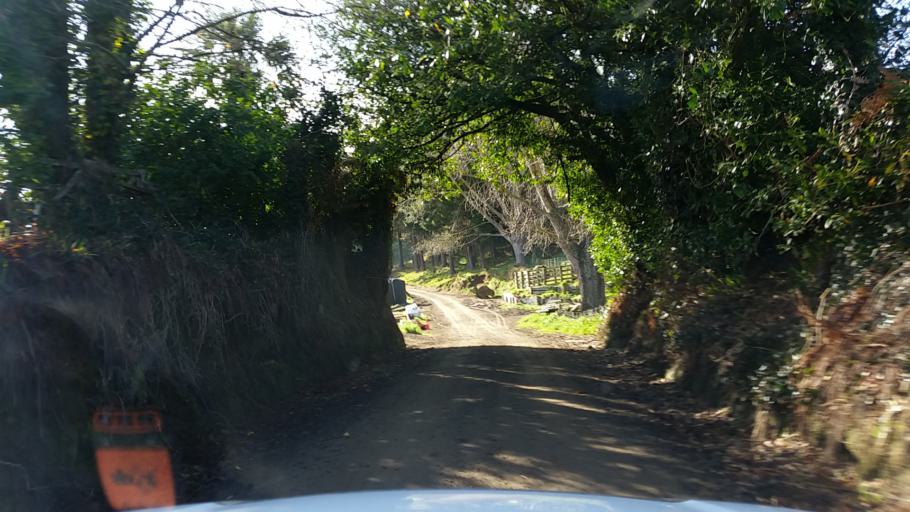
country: NZ
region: Taranaki
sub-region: South Taranaki District
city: Eltham
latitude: -39.3191
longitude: 174.5310
